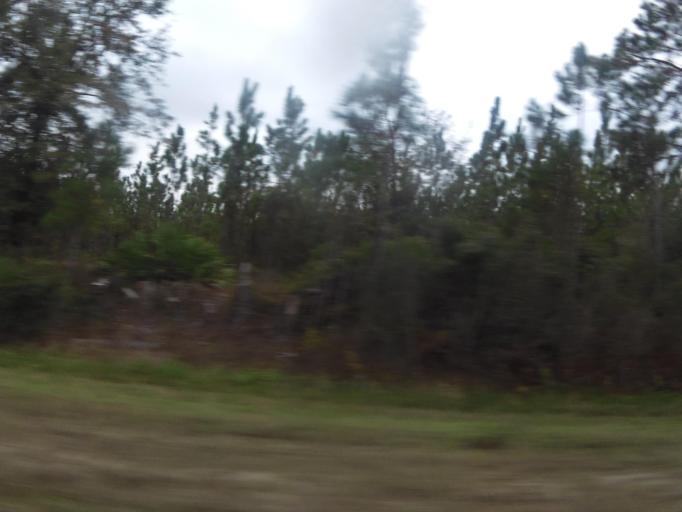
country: US
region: Georgia
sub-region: Charlton County
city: Folkston
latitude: 30.9050
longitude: -82.0683
